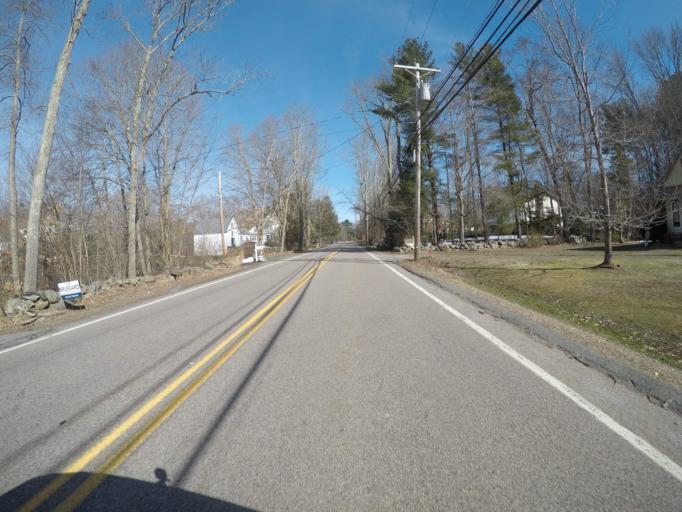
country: US
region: Massachusetts
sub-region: Bristol County
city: Easton
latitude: 42.0183
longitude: -71.1211
